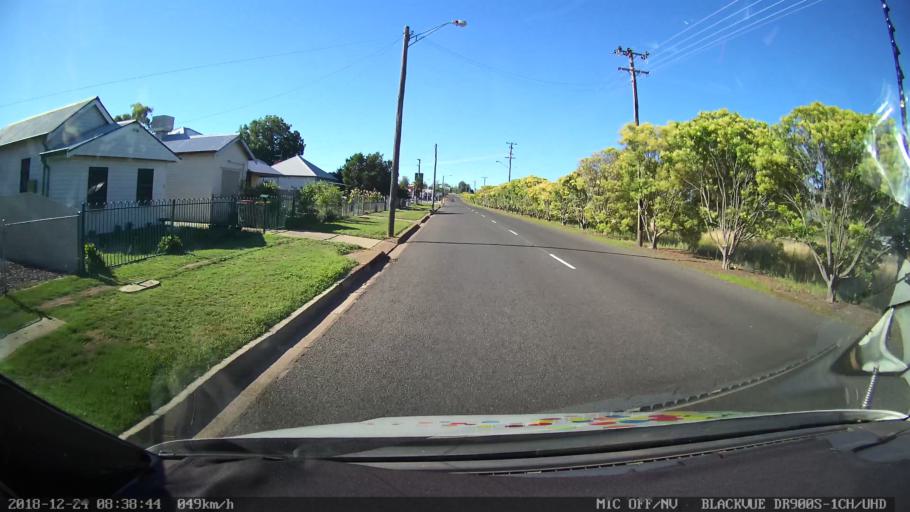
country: AU
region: New South Wales
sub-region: Liverpool Plains
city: Quirindi
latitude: -31.3430
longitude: 150.6476
